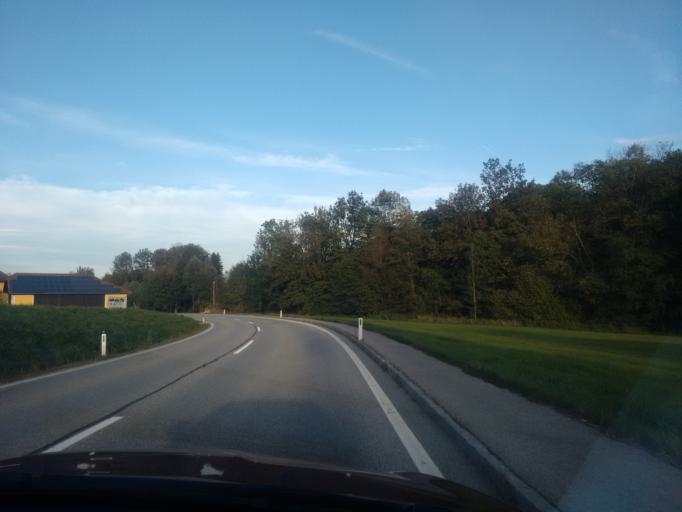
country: AT
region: Upper Austria
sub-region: Wels-Land
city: Bachmanning
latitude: 48.1707
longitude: 13.7578
